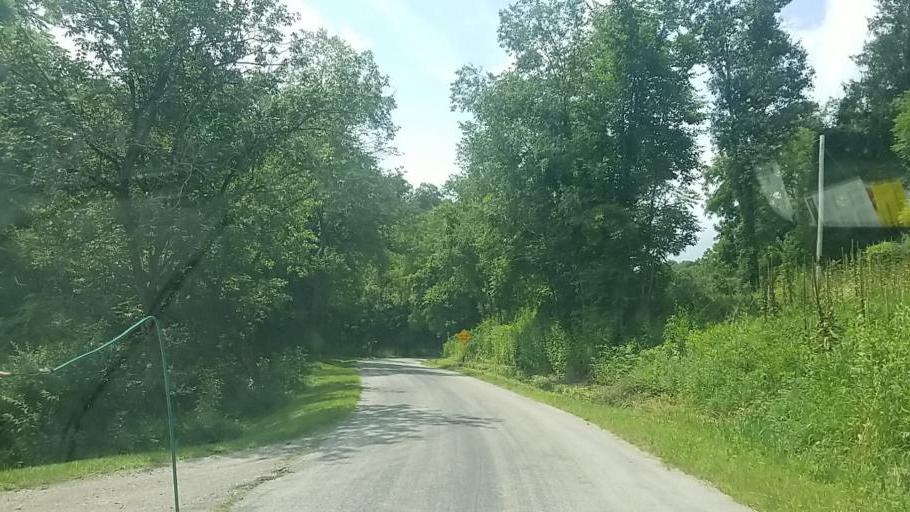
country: US
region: Ohio
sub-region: Muskingum County
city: Frazeysburg
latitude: 40.2219
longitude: -82.2359
